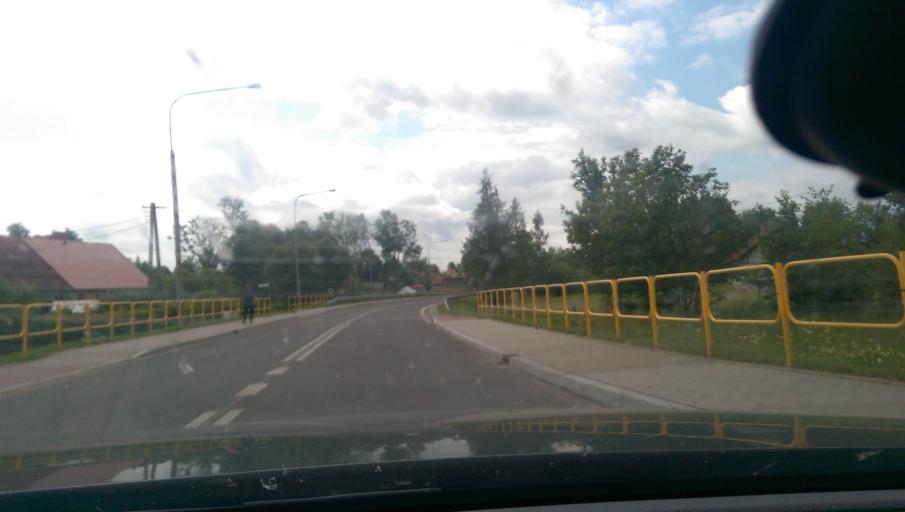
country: PL
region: Warmian-Masurian Voivodeship
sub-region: Powiat olecki
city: Kowale Oleckie
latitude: 54.2094
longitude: 22.4130
